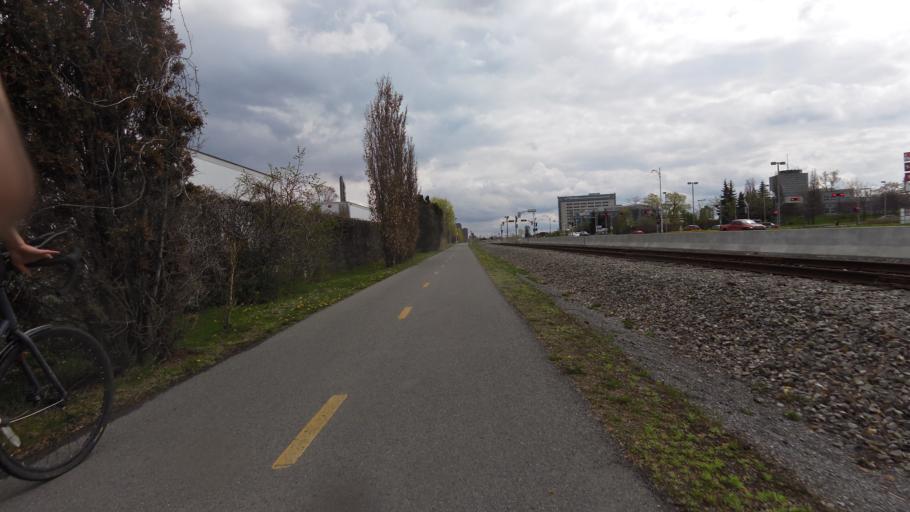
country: CA
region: Quebec
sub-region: Outaouais
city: Gatineau
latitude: 45.4498
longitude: -75.7285
